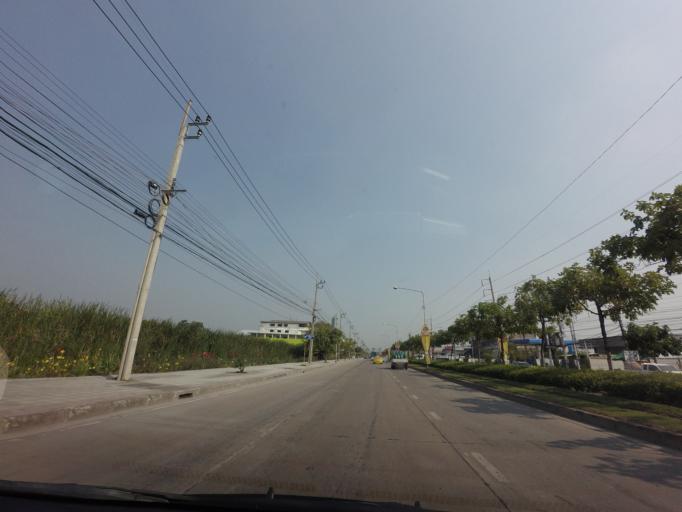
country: TH
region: Bangkok
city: Lat Krabang
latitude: 13.7515
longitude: 100.7868
